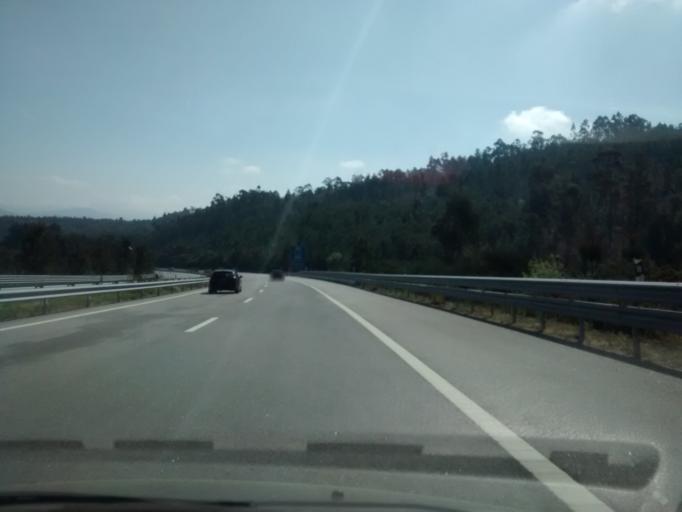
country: PT
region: Braga
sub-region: Cabeceiras de Basto
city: Cabeceiras de Basto
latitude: 41.4714
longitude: -7.9769
